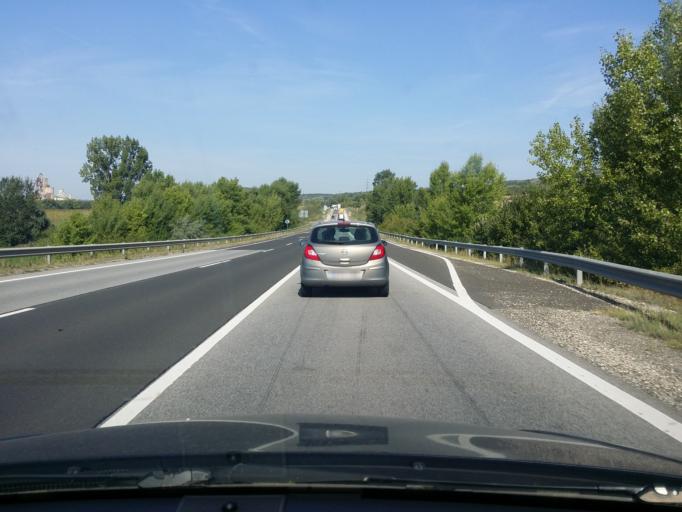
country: HU
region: Pest
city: Vac
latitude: 47.8071
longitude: 19.1269
